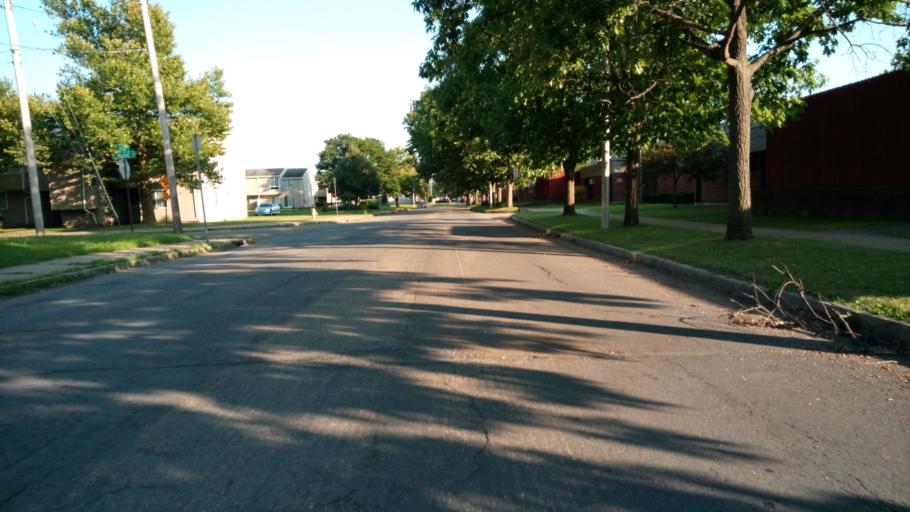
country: US
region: New York
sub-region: Chemung County
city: Elmira
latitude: 42.0929
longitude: -76.7934
